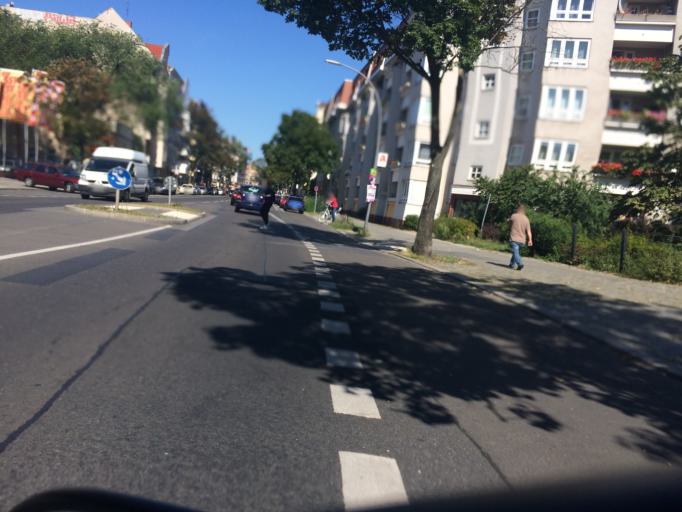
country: DE
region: Berlin
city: Gesundbrunnen
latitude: 52.5586
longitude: 13.3770
